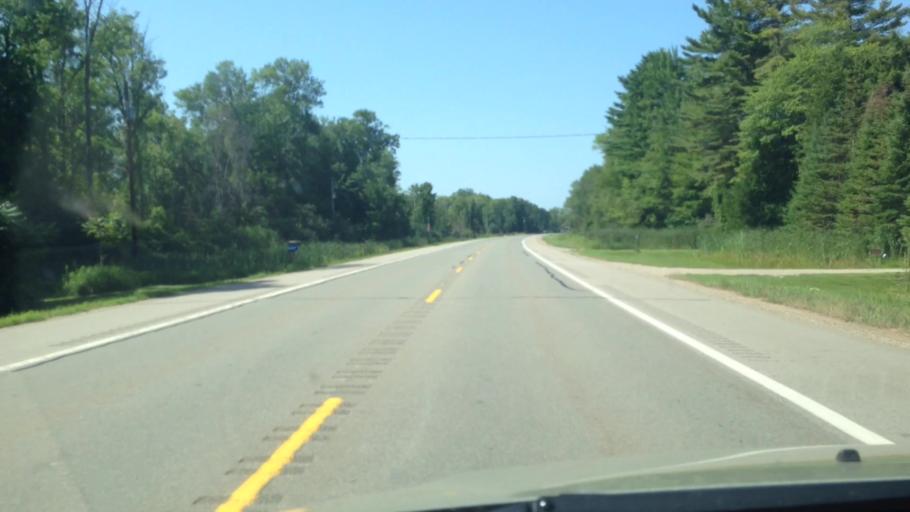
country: US
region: Michigan
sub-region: Menominee County
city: Menominee
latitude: 45.2178
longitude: -87.5191
